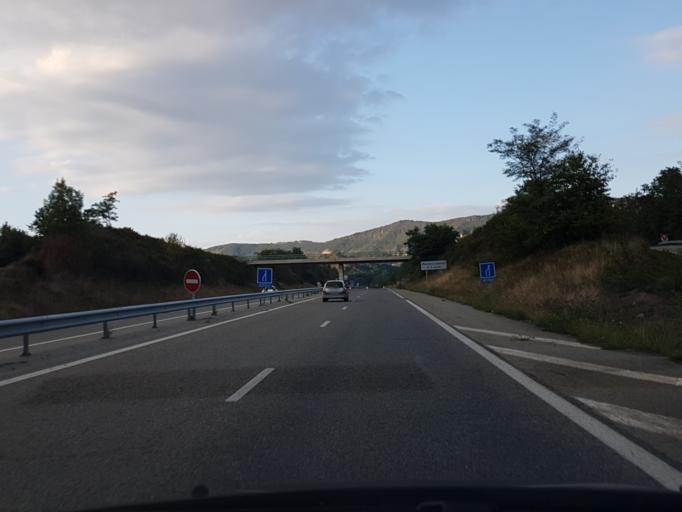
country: FR
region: Midi-Pyrenees
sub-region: Departement de l'Ariege
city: Saint-Paul-de-Jarrat
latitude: 42.9072
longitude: 1.6385
